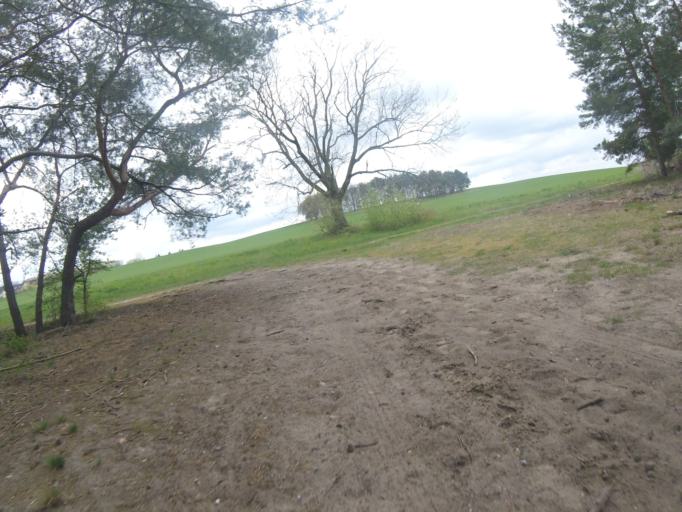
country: DE
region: Brandenburg
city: Konigs Wusterhausen
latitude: 52.2638
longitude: 13.5996
